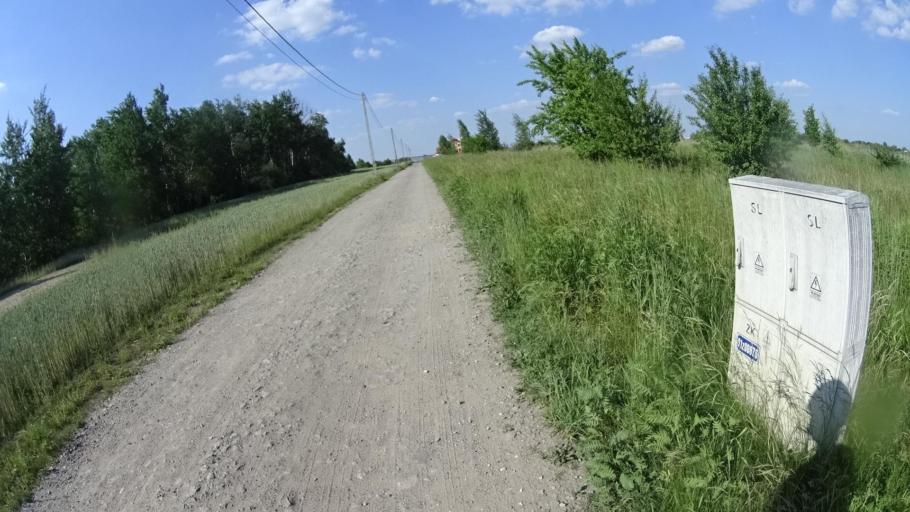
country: PL
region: Masovian Voivodeship
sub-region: Powiat warszawski zachodni
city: Ozarow Mazowiecki
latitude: 52.1923
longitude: 20.7625
